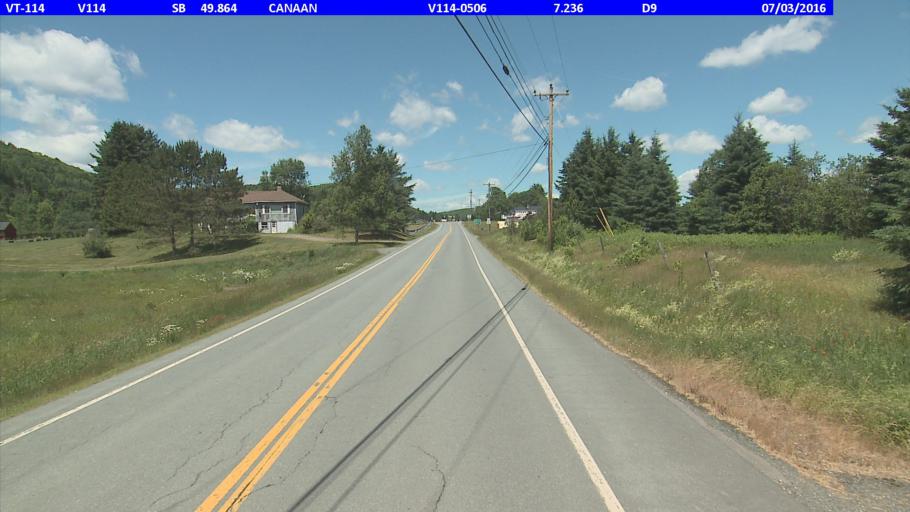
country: US
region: New Hampshire
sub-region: Coos County
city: Colebrook
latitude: 45.0045
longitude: -71.5535
